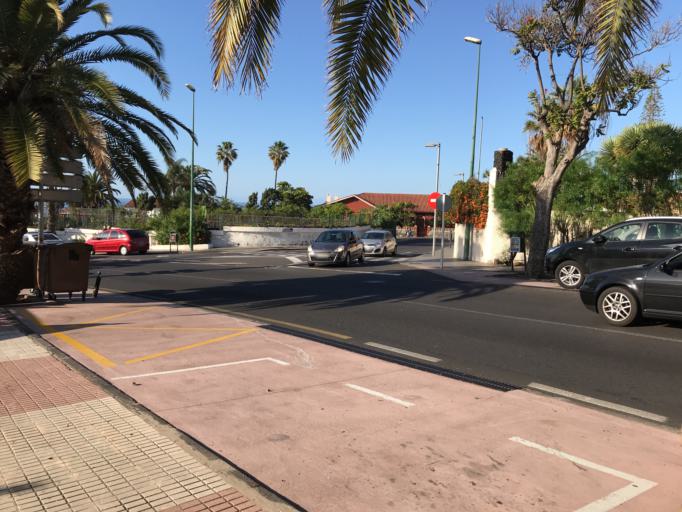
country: ES
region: Canary Islands
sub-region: Provincia de Santa Cruz de Tenerife
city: Puerto de la Cruz
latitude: 28.4143
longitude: -16.5399
